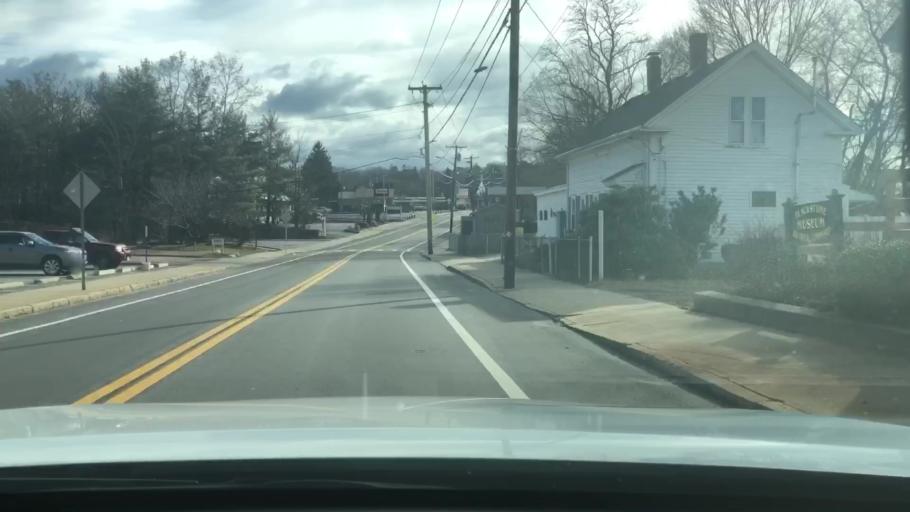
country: US
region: Massachusetts
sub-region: Worcester County
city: Blackstone
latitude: 42.0171
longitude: -71.5299
